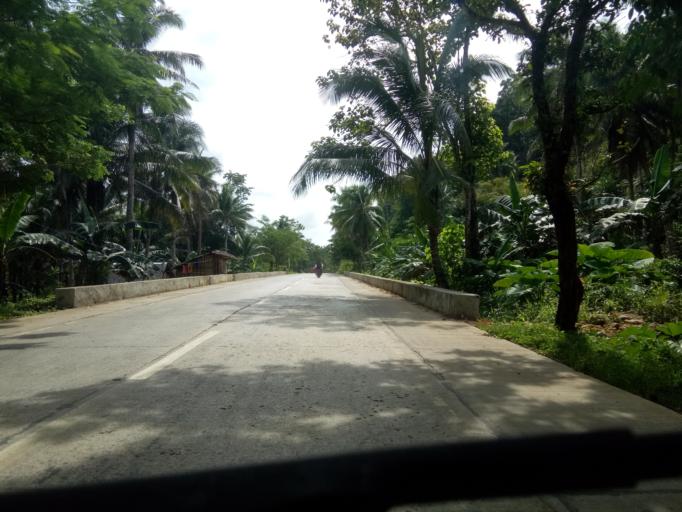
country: PH
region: Caraga
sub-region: Province of Surigao del Norte
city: Dapa
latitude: 9.7675
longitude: 126.0612
